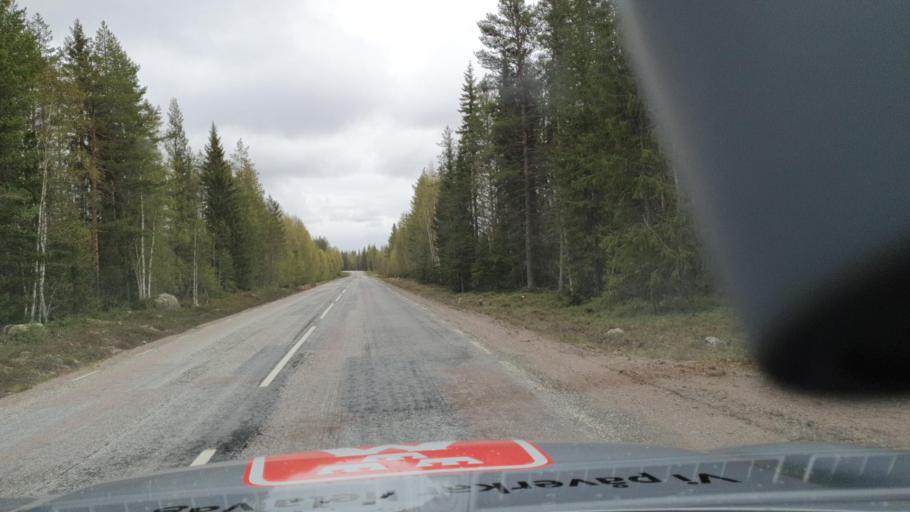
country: SE
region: Vaesternorrland
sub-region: Solleftea Kommun
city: Solleftea
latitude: 63.6550
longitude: 17.3211
